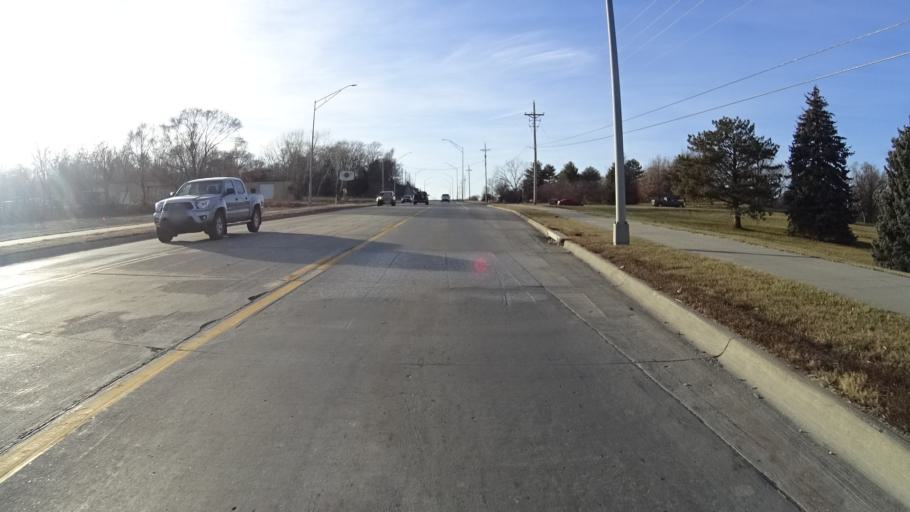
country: US
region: Nebraska
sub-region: Sarpy County
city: La Vista
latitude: 41.1908
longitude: -96.0163
